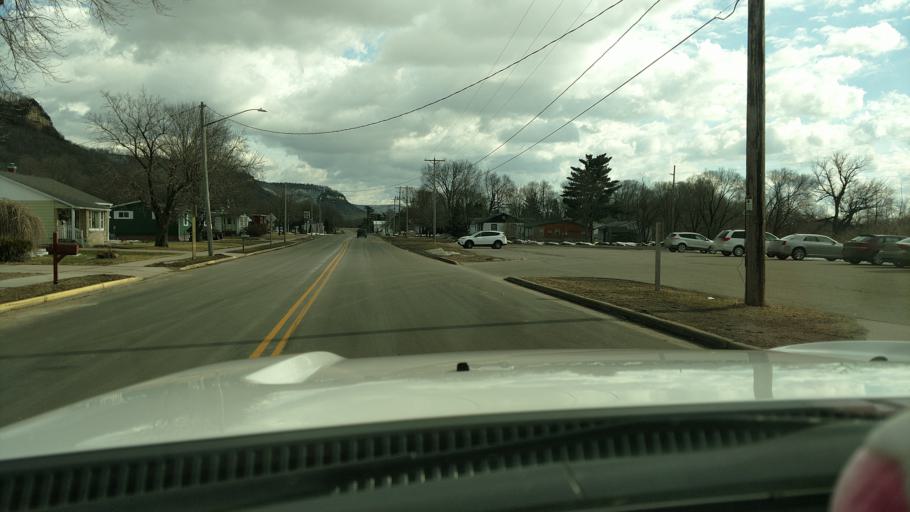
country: US
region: Minnesota
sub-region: Wabasha County
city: Wabasha
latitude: 44.4188
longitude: -92.0063
